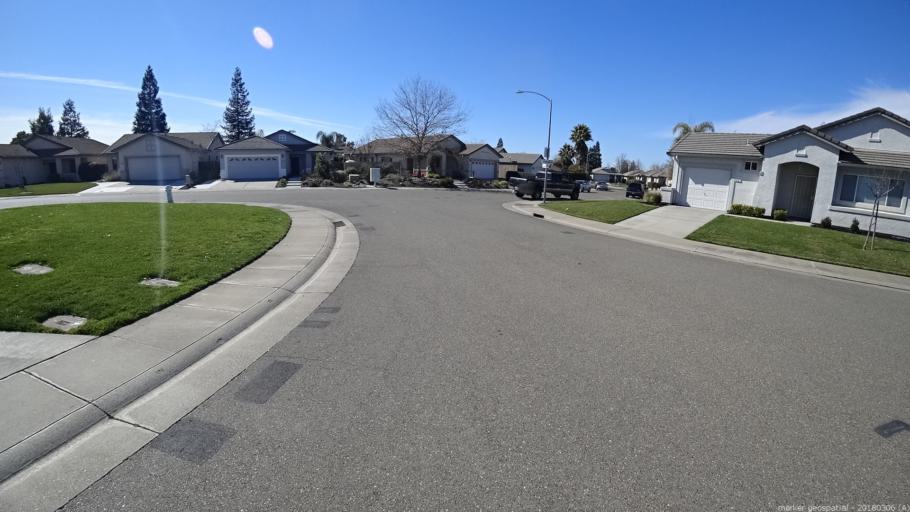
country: US
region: California
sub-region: Sacramento County
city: Vineyard
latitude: 38.4626
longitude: -121.3547
